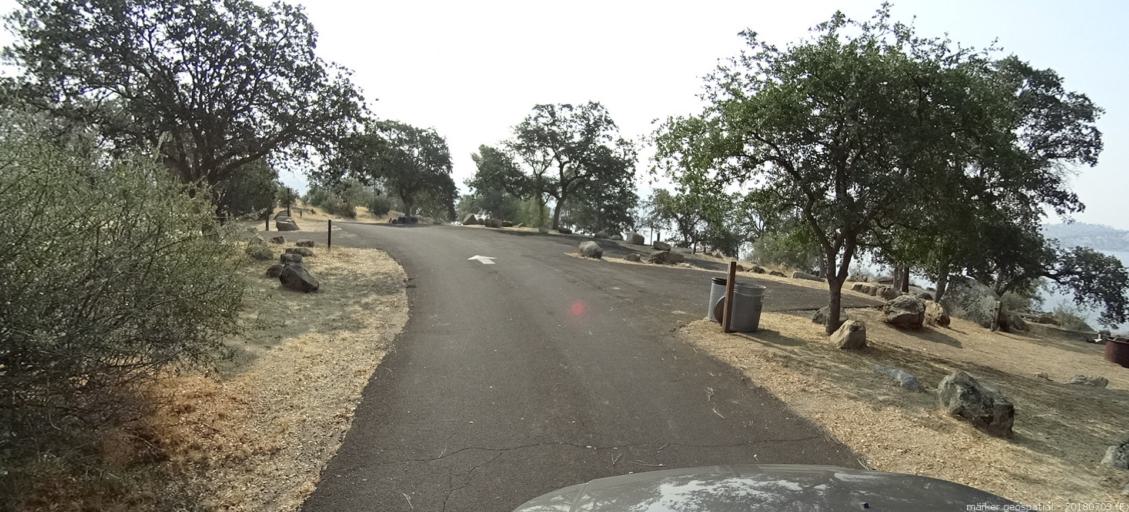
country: US
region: California
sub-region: Madera County
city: Yosemite Lakes
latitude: 37.0224
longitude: -119.6824
